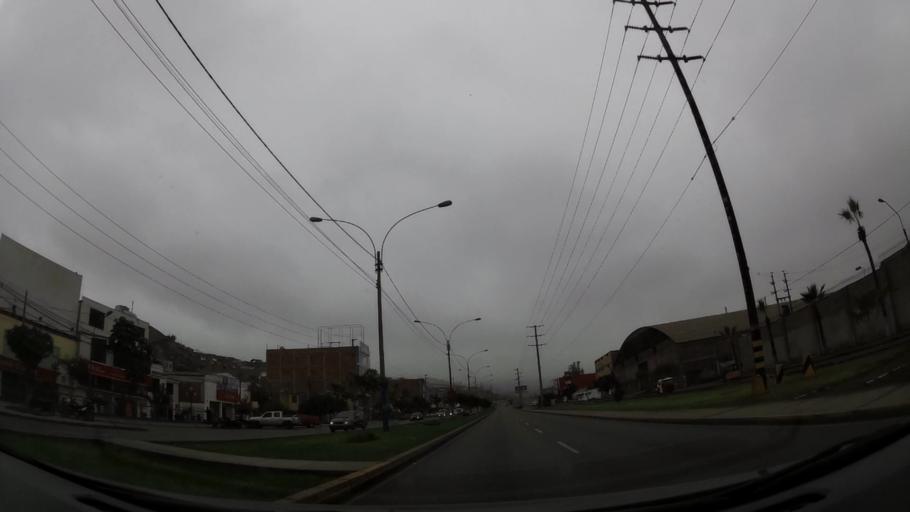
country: PE
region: Lima
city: Ventanilla
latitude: -11.8706
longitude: -77.1276
